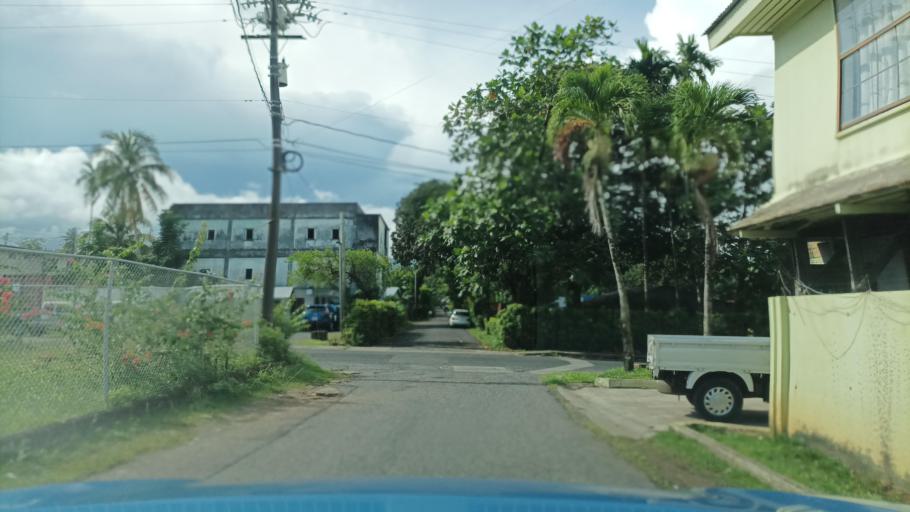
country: FM
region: Pohnpei
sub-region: Kolonia Municipality
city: Kolonia
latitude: 6.9659
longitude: 158.2110
